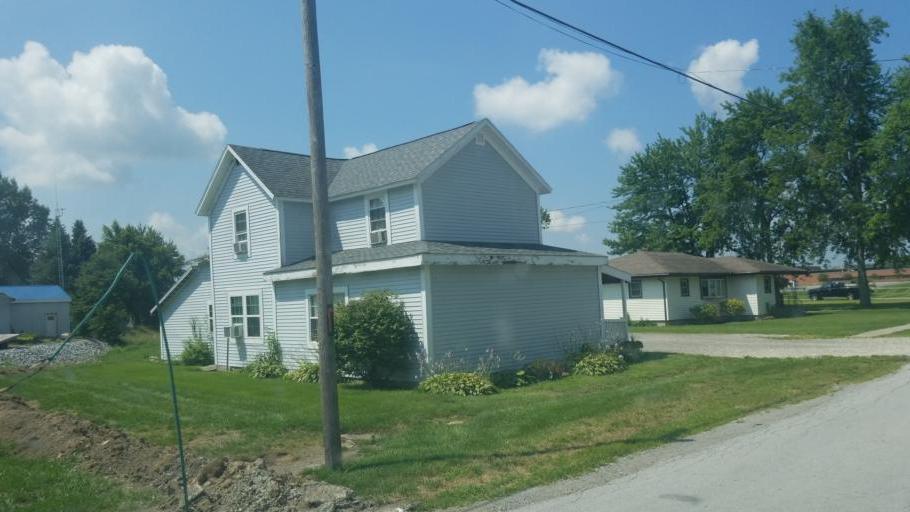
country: US
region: Ohio
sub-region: Hardin County
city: Ada
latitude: 40.7065
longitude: -83.9225
